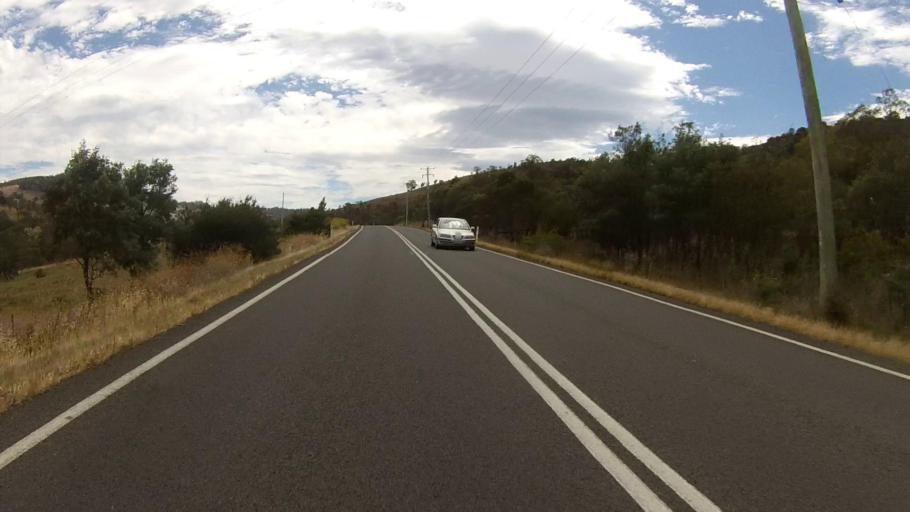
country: AU
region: Tasmania
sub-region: Brighton
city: Old Beach
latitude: -42.6866
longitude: 147.3524
